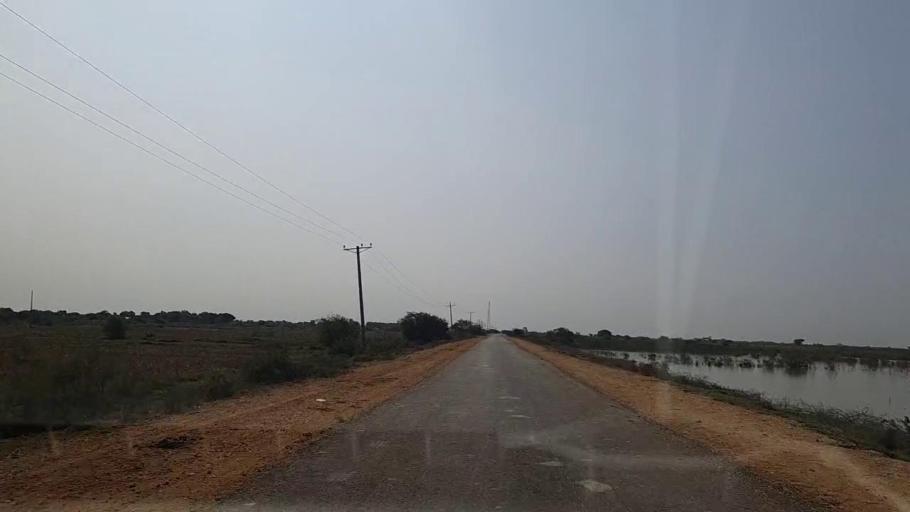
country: PK
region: Sindh
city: Chuhar Jamali
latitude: 24.2939
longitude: 67.9284
